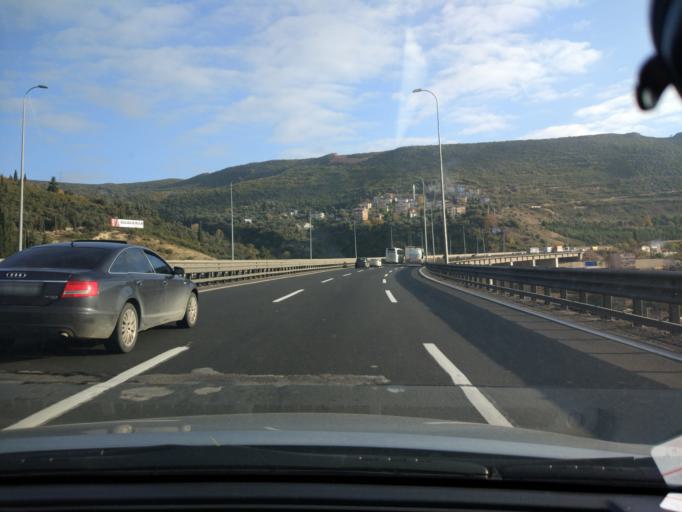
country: TR
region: Kocaeli
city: Hereke
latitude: 40.7873
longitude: 29.6118
